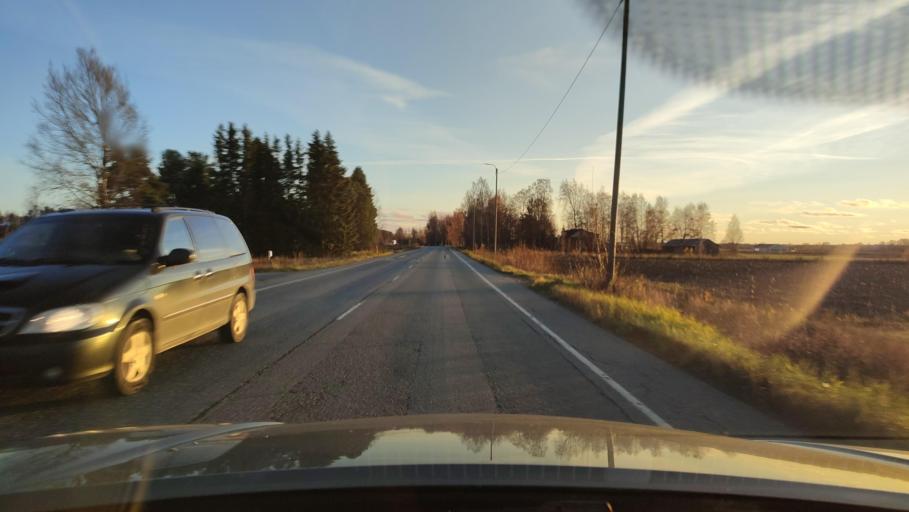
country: FI
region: Ostrobothnia
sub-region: Sydosterbotten
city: Naerpes
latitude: 62.4557
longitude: 21.3540
